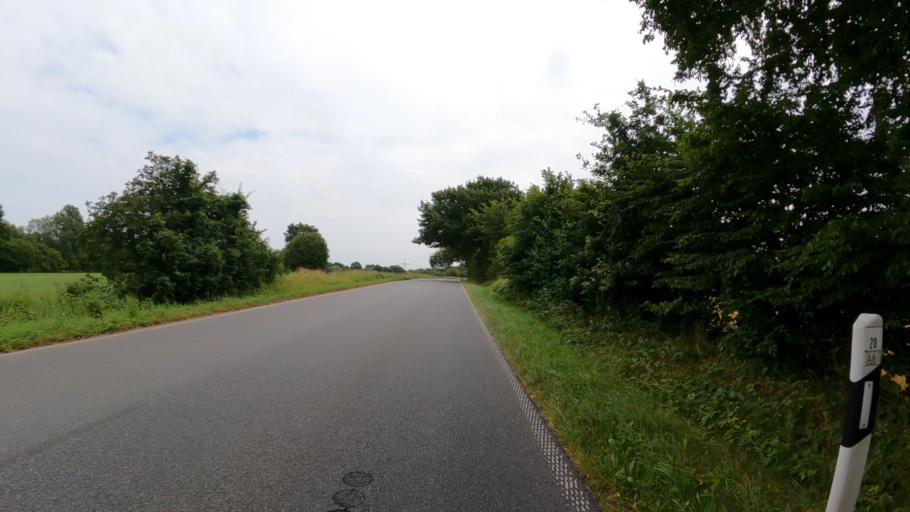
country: DE
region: Schleswig-Holstein
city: Mozen
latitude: 53.9227
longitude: 10.2527
